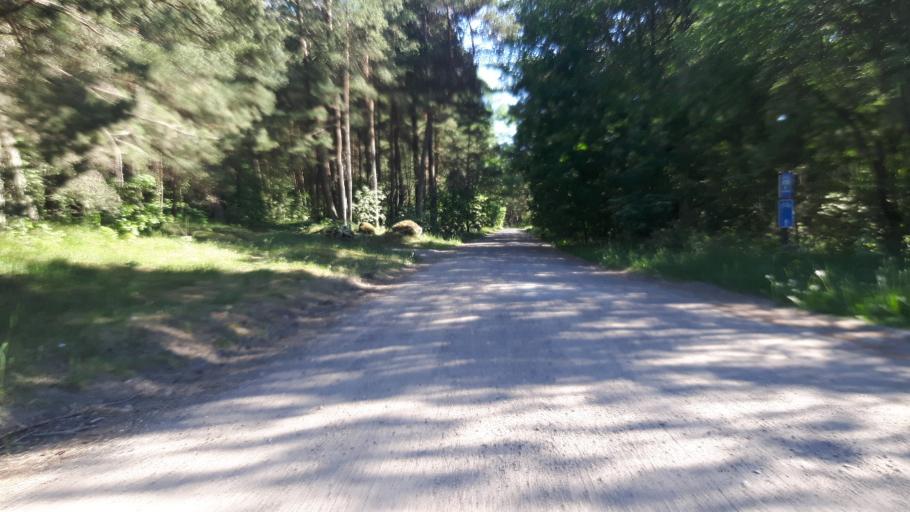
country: LV
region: Salacgrivas
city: Salacgriva
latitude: 57.7433
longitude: 24.3524
